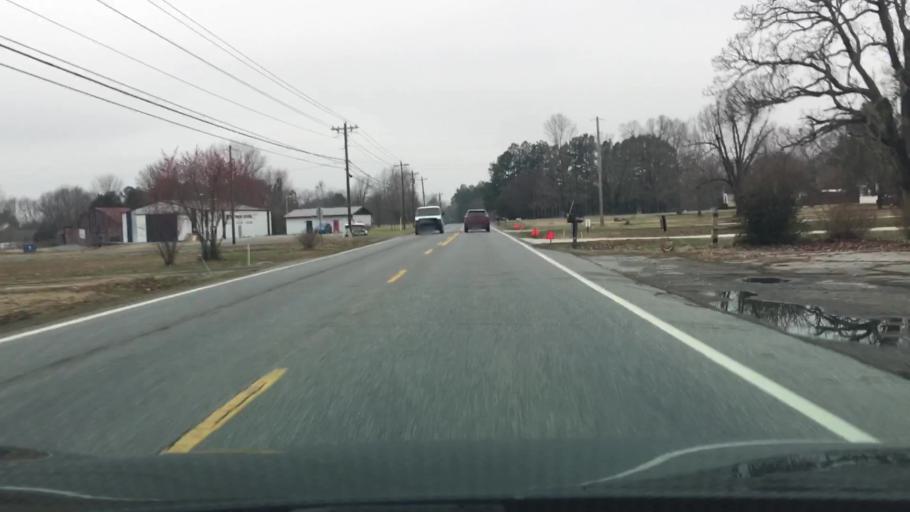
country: US
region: Kentucky
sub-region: Marshall County
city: Calvert City
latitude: 36.9715
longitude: -88.4121
